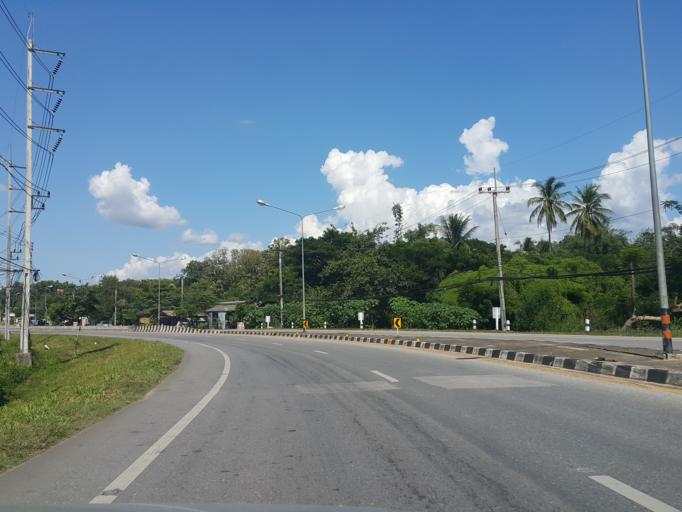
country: TH
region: Chiang Mai
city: Mae Taeng
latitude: 19.1257
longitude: 98.9485
